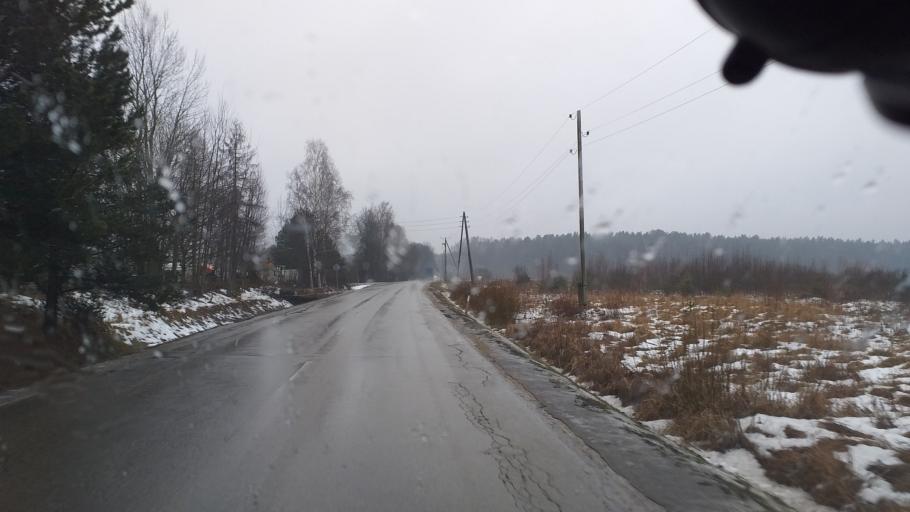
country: LV
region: Babite
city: Pinki
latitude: 56.9685
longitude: 23.9680
